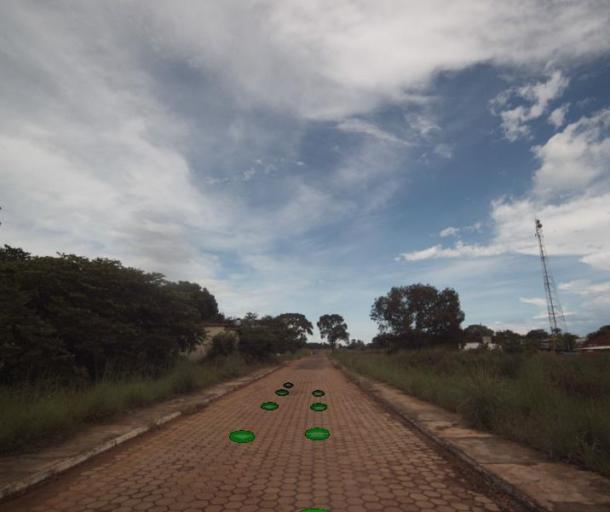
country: BR
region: Goias
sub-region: Sao Miguel Do Araguaia
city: Sao Miguel do Araguaia
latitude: -13.2165
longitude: -50.5756
